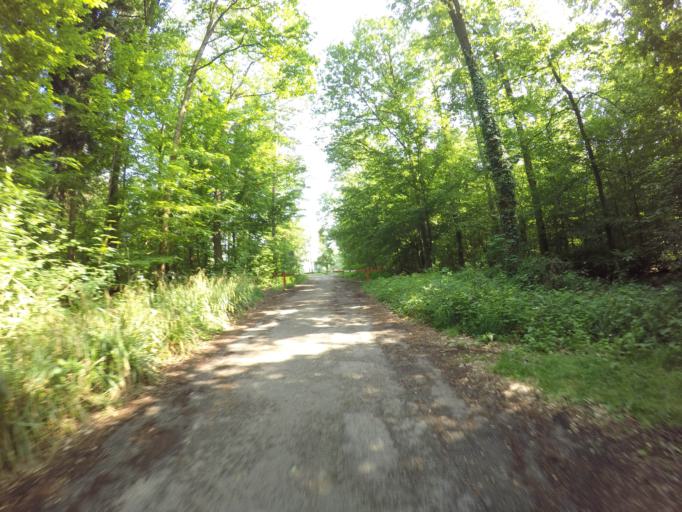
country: DE
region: Baden-Wuerttemberg
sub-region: Tuebingen Region
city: Kusterdingen
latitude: 48.5134
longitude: 9.0992
